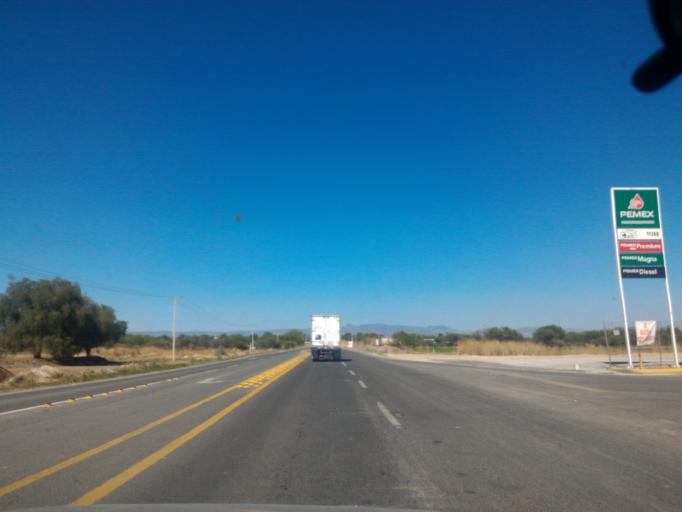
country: MX
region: Guanajuato
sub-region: San Francisco del Rincon
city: San Roque de Montes
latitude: 21.0260
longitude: -101.7841
